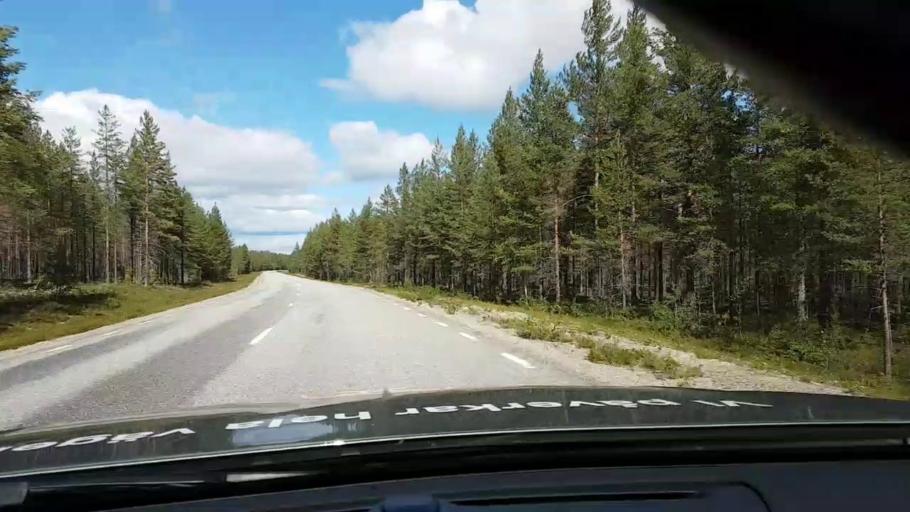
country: SE
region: Vaesternorrland
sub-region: OErnskoeldsviks Kommun
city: Bredbyn
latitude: 63.6169
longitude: 17.9070
